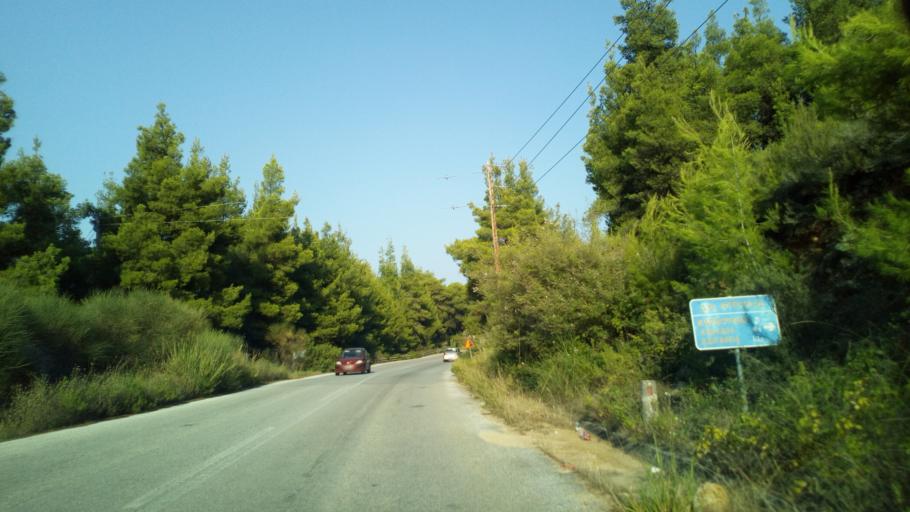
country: GR
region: Central Macedonia
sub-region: Nomos Chalkidikis
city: Neos Marmaras
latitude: 40.1798
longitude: 23.8244
